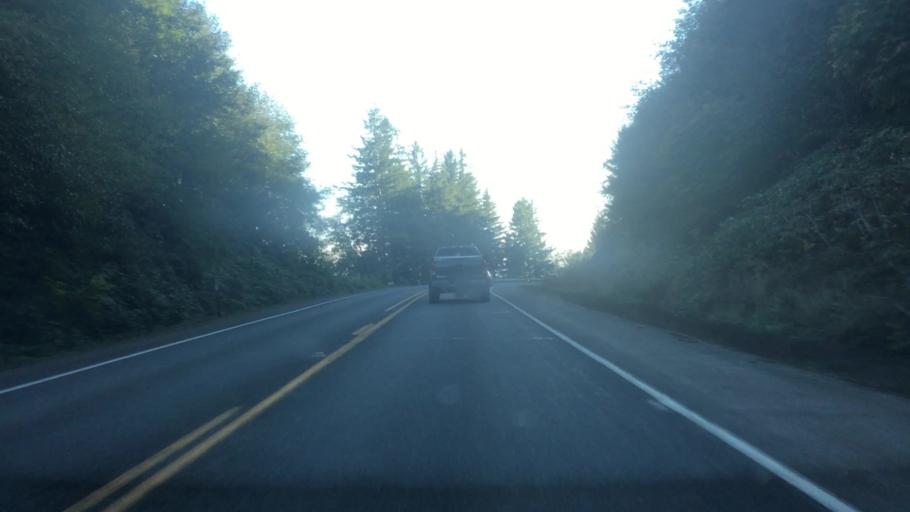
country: US
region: Oregon
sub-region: Clatsop County
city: Astoria
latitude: 46.2568
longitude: -123.8530
